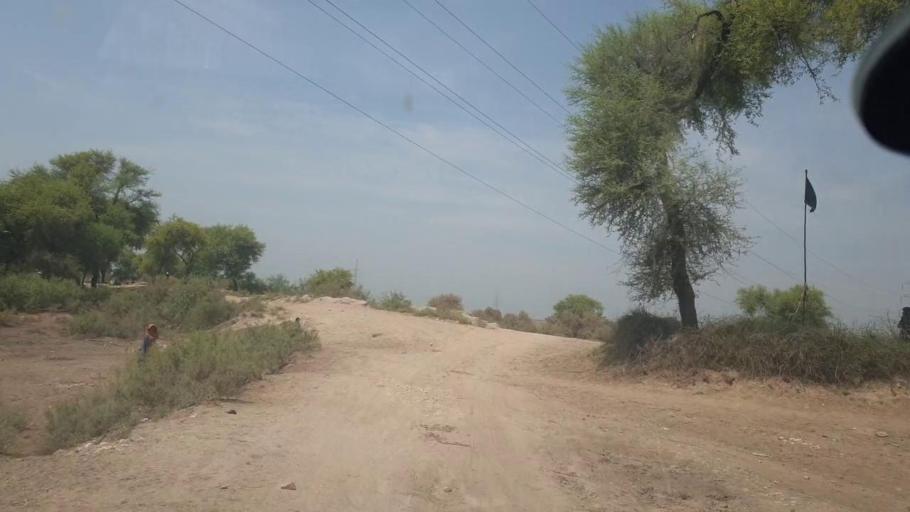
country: PK
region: Sindh
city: Thul
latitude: 28.1819
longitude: 68.6147
